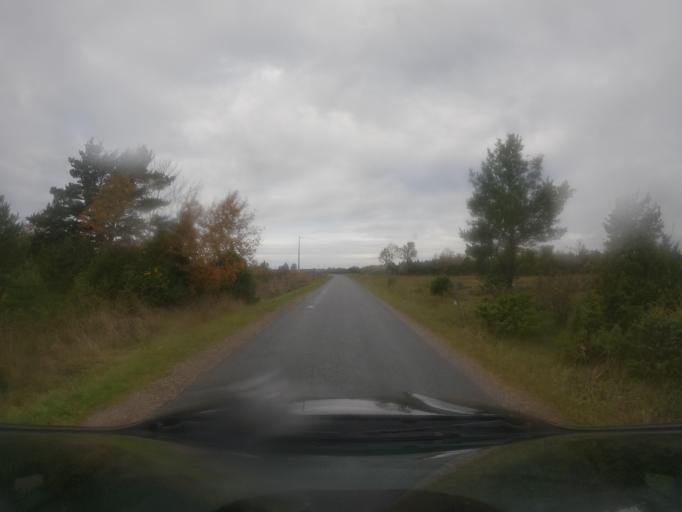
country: EE
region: Saare
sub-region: Kuressaare linn
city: Kuressaare
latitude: 58.4432
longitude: 21.9834
